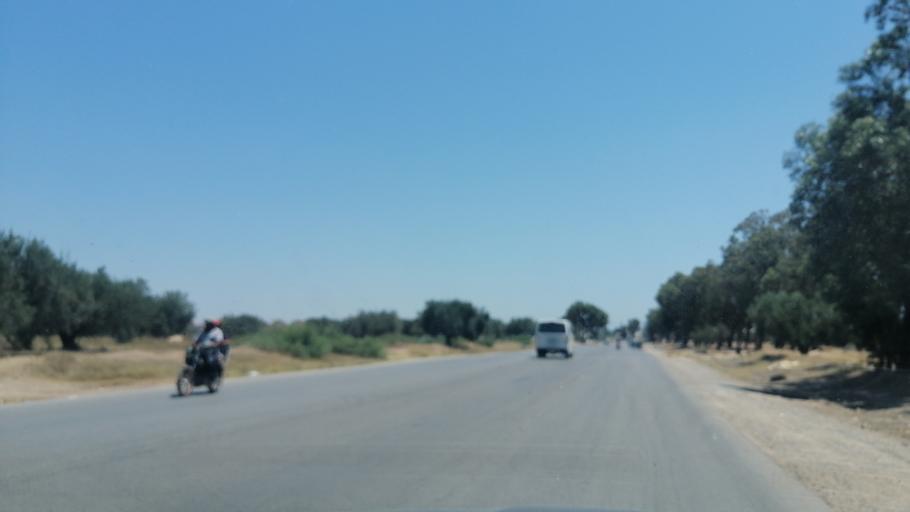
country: TN
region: Al Qayrawan
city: Sbikha
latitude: 36.1205
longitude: 10.0845
